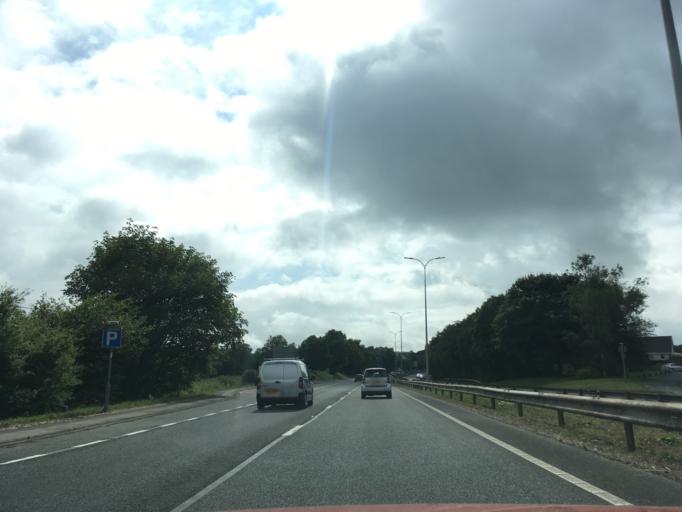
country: GB
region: Wales
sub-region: Carmarthenshire
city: Saint Clears
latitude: 51.8204
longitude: -4.4899
